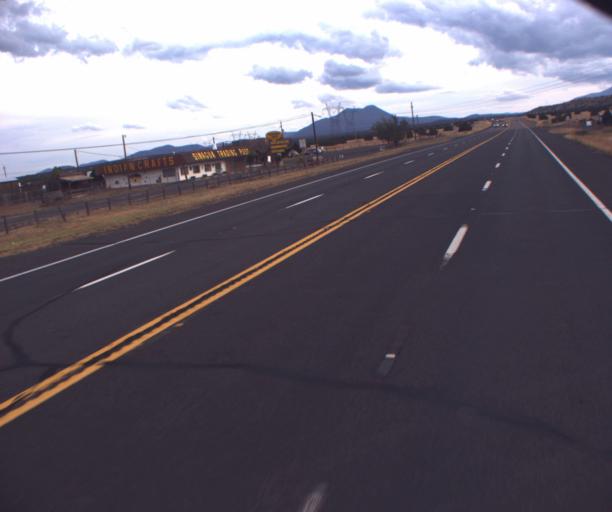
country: US
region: Arizona
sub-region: Coconino County
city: Flagstaff
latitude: 35.5413
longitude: -111.5390
